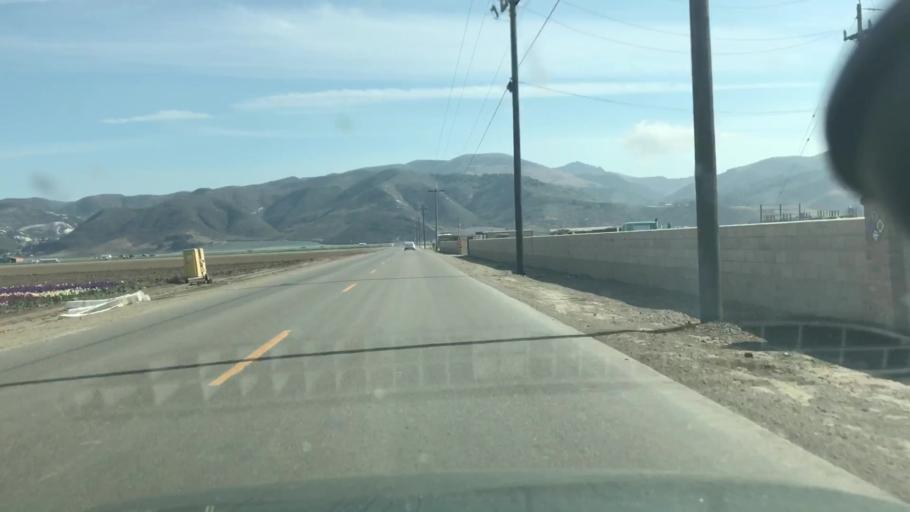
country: US
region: California
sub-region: Santa Barbara County
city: Lompoc
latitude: 34.6516
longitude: -120.4930
